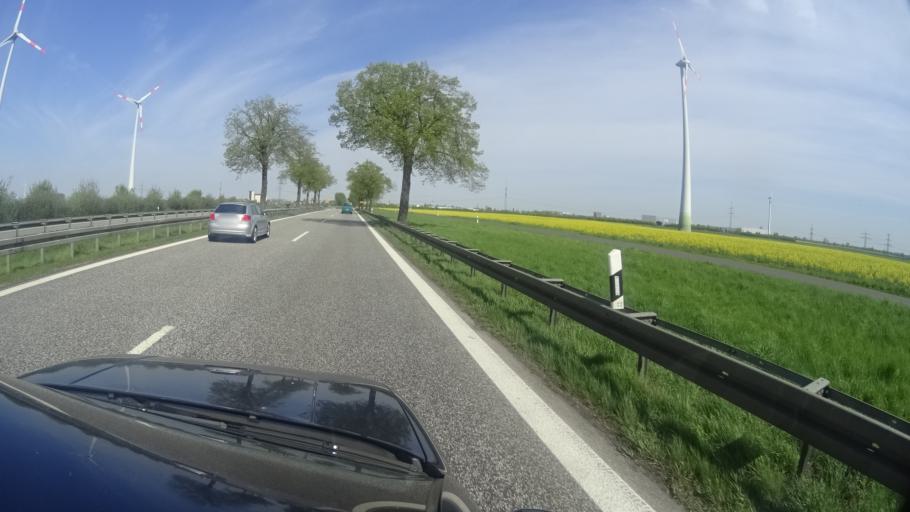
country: DE
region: Brandenburg
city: Nauen
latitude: 52.5877
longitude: 12.8965
